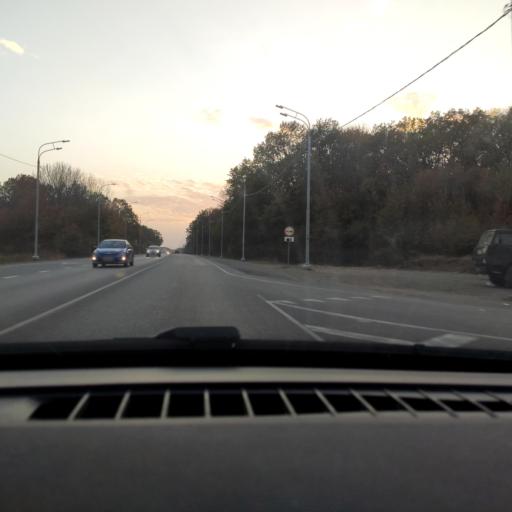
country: RU
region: Voronezj
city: Semiluki
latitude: 51.6491
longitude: 39.0297
